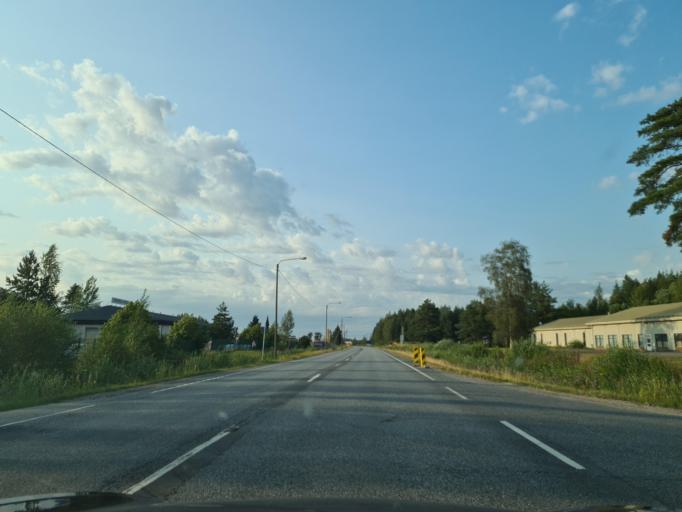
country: FI
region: Southern Ostrobothnia
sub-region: Seinaejoki
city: Kauhava
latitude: 63.0816
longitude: 23.0586
